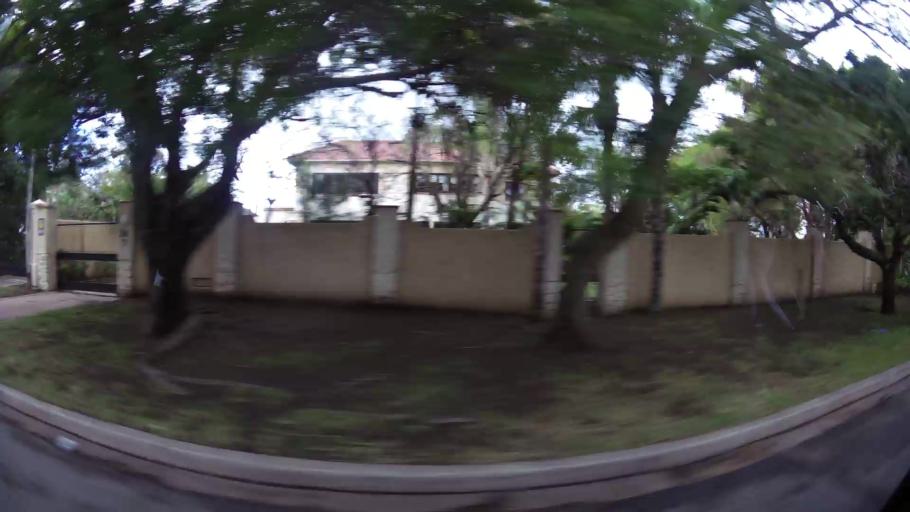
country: ZA
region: Eastern Cape
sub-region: Nelson Mandela Bay Metropolitan Municipality
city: Port Elizabeth
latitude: -33.9616
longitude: 25.5908
